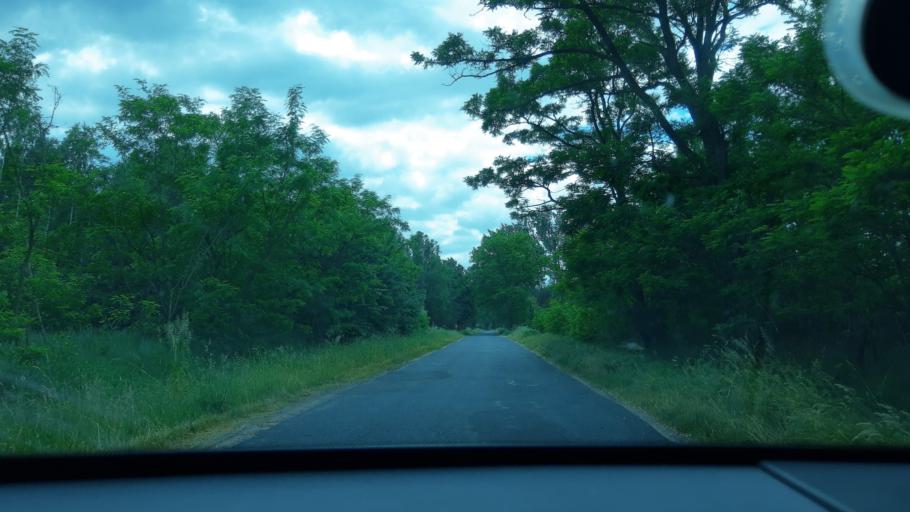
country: PL
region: Lodz Voivodeship
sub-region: Powiat sieradzki
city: Burzenin
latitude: 51.5019
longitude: 18.8468
